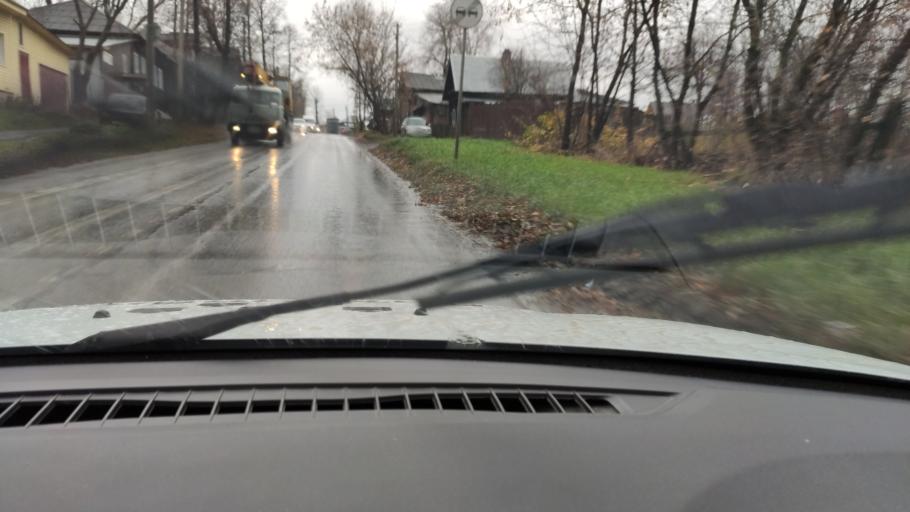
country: RU
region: Perm
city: Perm
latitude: 58.0394
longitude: 56.3281
